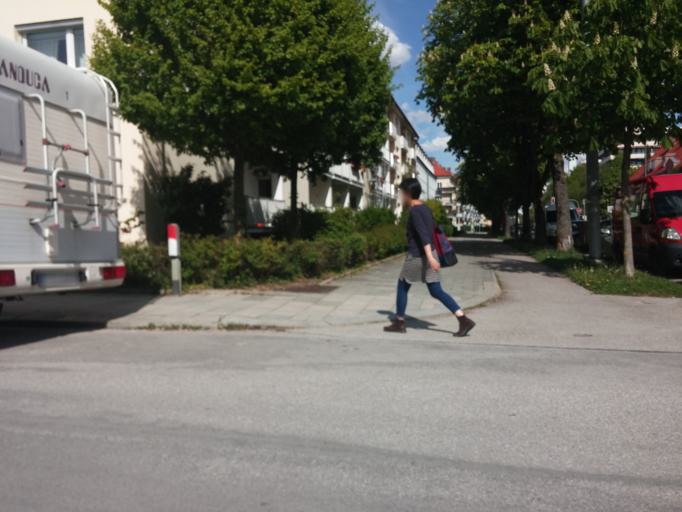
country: DE
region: Bavaria
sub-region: Upper Bavaria
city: Pullach im Isartal
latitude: 48.1127
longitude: 11.5245
